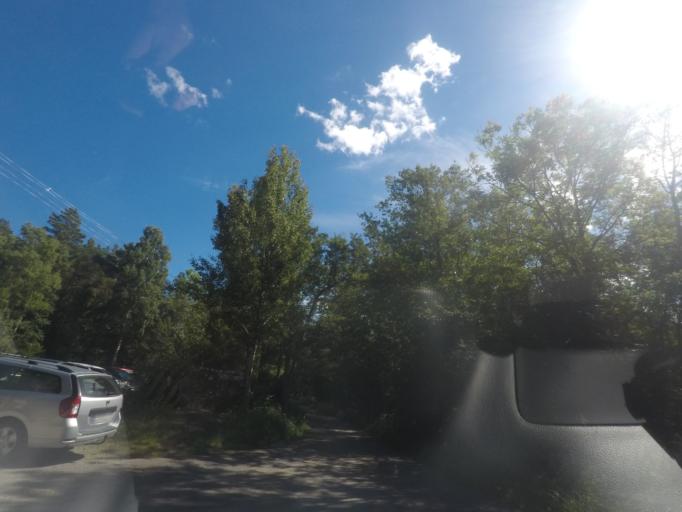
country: SE
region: Stockholm
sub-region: Norrtalje Kommun
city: Arno
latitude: 60.2161
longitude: 18.7273
